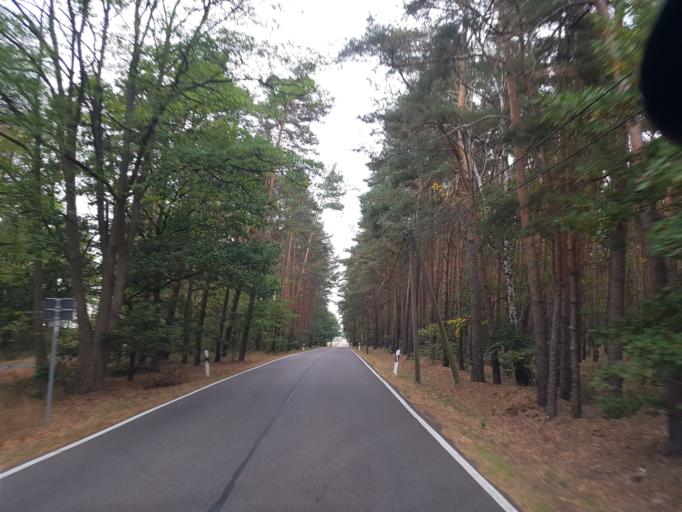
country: DE
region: Brandenburg
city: Bronkow
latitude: 51.7248
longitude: 13.8569
